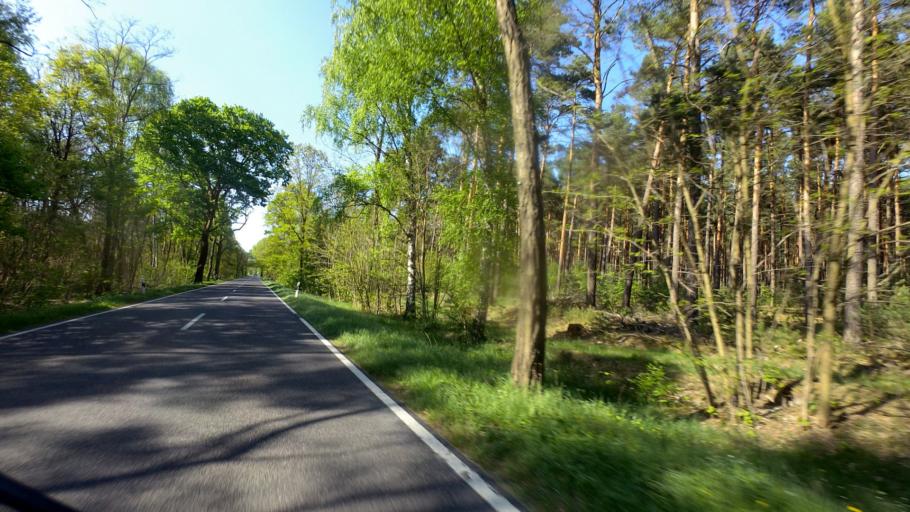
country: DE
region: Brandenburg
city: Gross Koris
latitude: 52.1802
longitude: 13.7108
